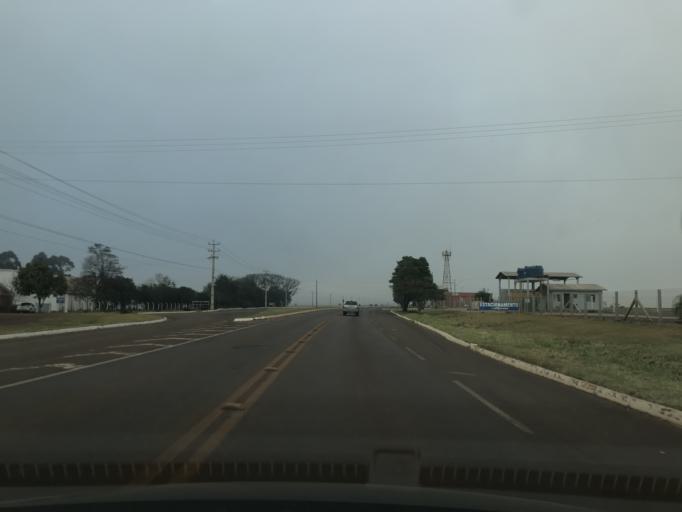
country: BR
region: Parana
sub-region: Toledo
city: Toledo
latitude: -24.6834
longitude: -53.6958
